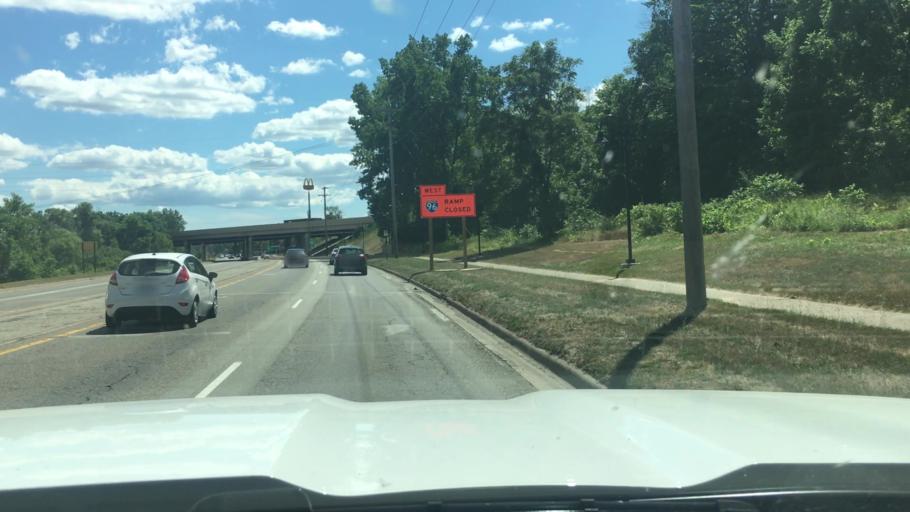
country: US
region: Michigan
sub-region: Kent County
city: Comstock Park
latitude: 43.0430
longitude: -85.6602
